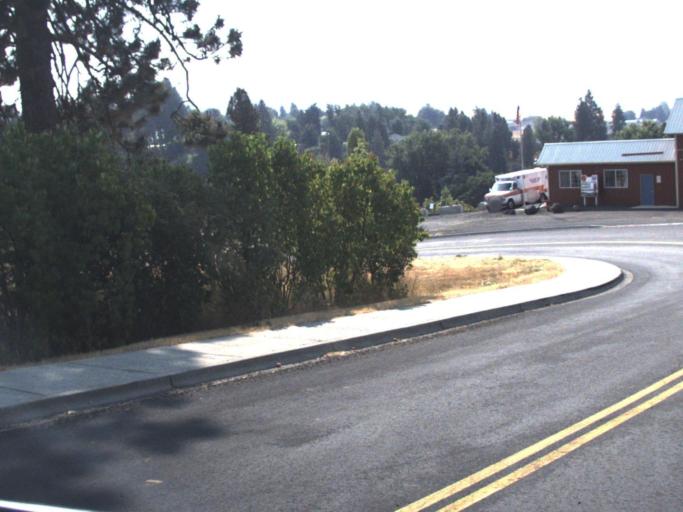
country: US
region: Idaho
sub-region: Latah County
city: Moscow
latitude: 46.9113
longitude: -117.0799
